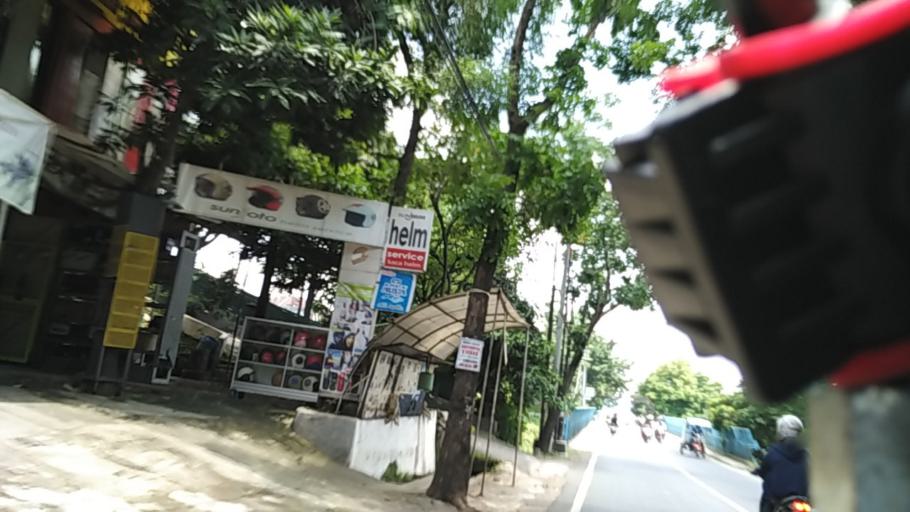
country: ID
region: Central Java
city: Semarang
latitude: -7.0113
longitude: 110.3818
